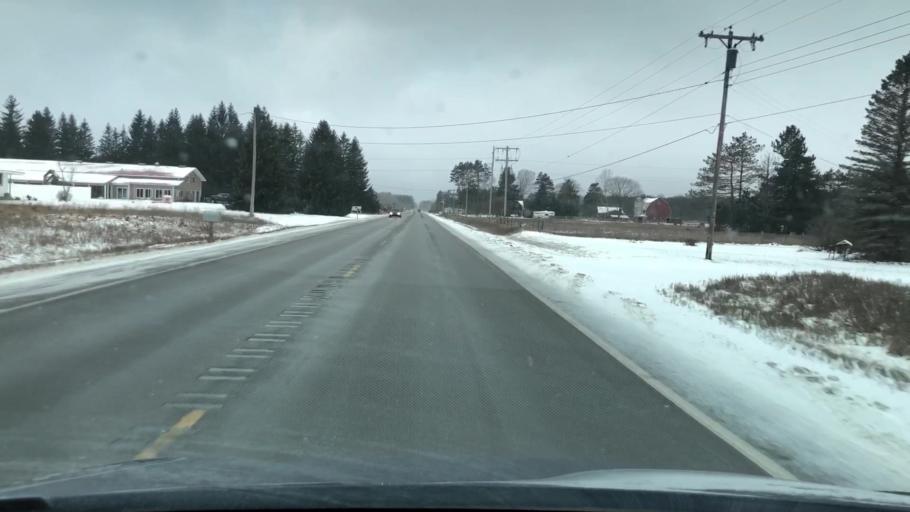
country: US
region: Michigan
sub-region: Wexford County
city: Cadillac
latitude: 44.2813
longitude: -85.4438
